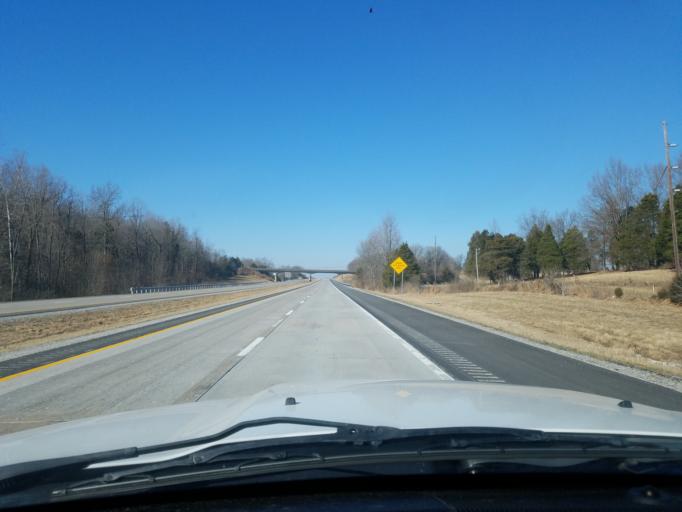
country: US
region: Kentucky
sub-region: Ohio County
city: Beaver Dam
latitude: 37.4066
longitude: -86.8253
